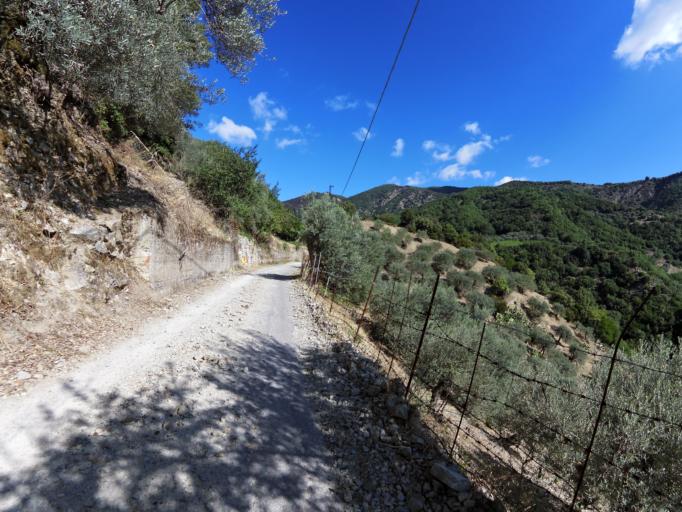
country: IT
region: Calabria
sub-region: Provincia di Reggio Calabria
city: Bivongi
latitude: 38.4869
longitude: 16.4258
